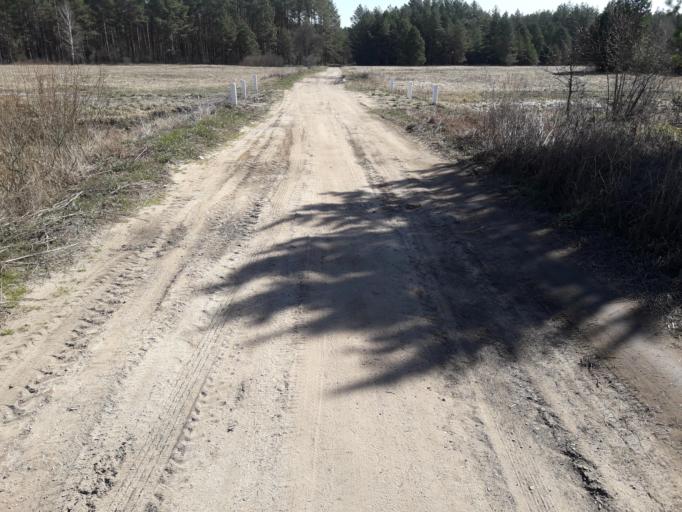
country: LT
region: Alytaus apskritis
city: Druskininkai
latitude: 54.0958
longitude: 24.1319
